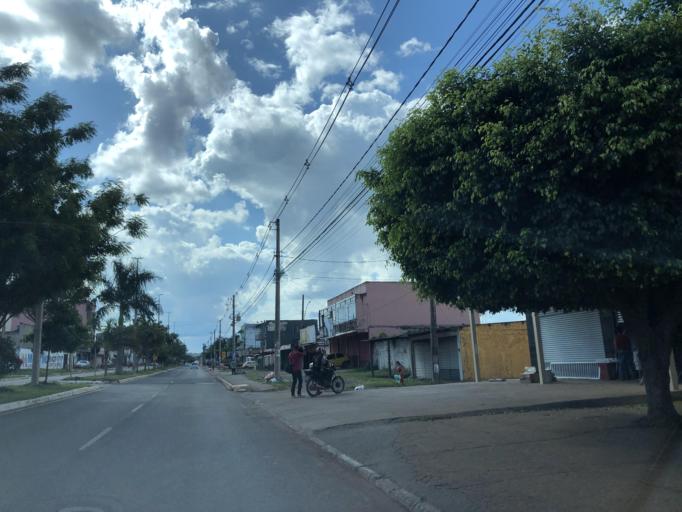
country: BR
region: Federal District
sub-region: Brasilia
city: Brasilia
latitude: -15.8948
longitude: -47.7767
